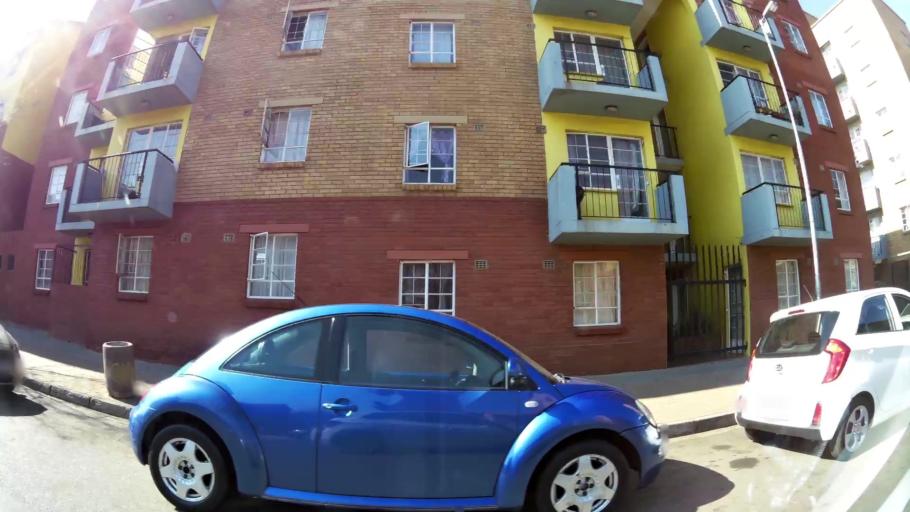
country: ZA
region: Gauteng
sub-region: City of Johannesburg Metropolitan Municipality
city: Johannesburg
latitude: -26.2003
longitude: 28.0338
